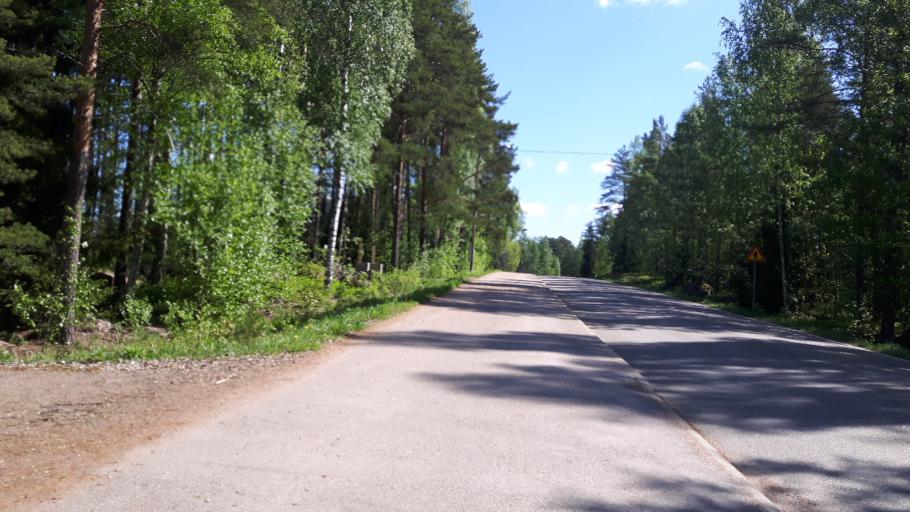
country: FI
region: Kymenlaakso
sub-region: Kotka-Hamina
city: Virolahti
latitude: 60.5161
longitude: 27.4546
